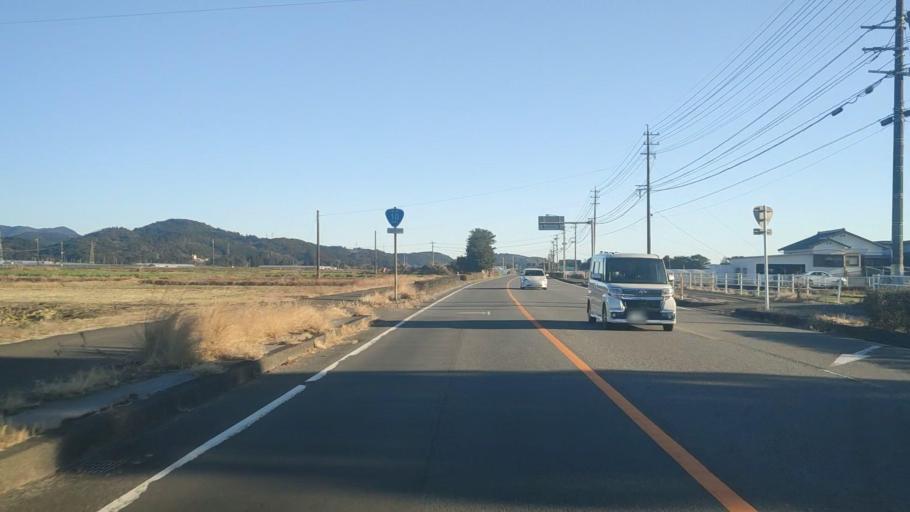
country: JP
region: Miyazaki
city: Takanabe
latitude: 32.3179
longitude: 131.5920
